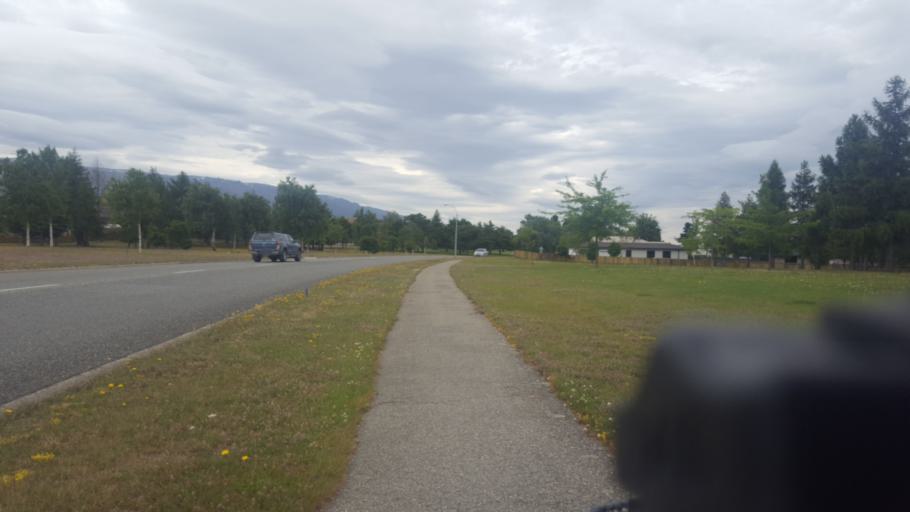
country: NZ
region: Otago
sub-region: Queenstown-Lakes District
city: Wanaka
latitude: -45.0490
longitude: 169.1846
